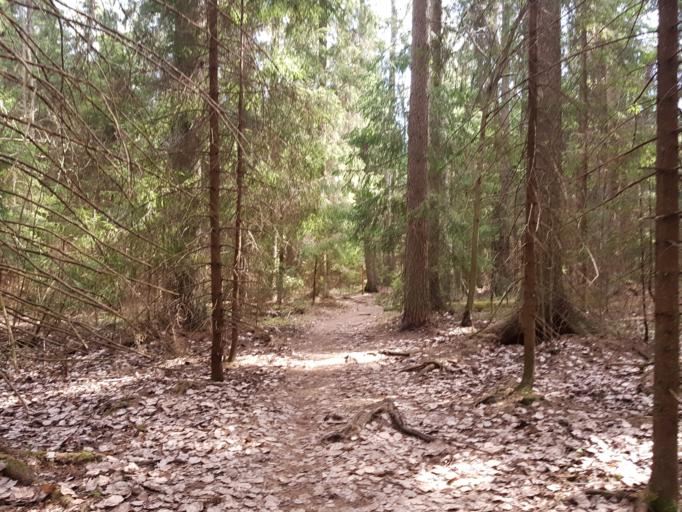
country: FI
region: Uusimaa
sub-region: Helsinki
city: Helsinki
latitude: 60.2583
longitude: 24.9249
